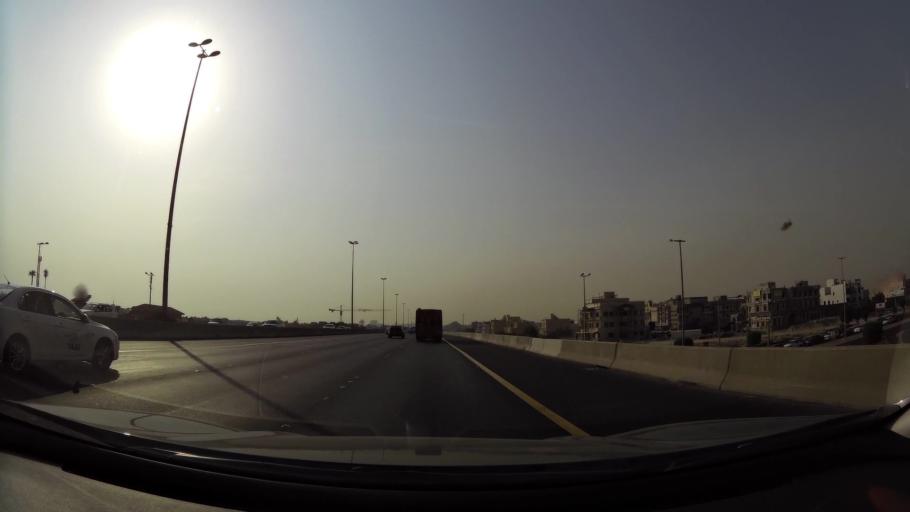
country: KW
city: Al Funaytis
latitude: 29.2131
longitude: 48.1031
